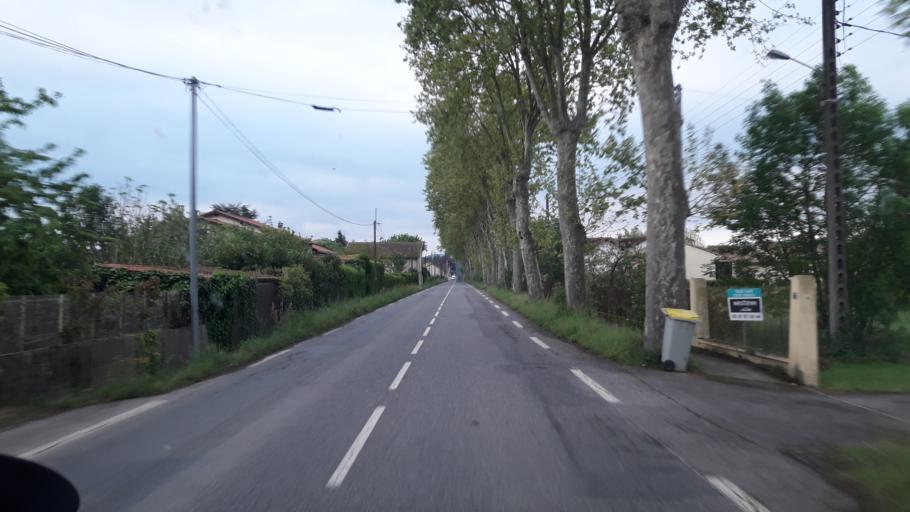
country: FR
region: Midi-Pyrenees
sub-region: Departement de la Haute-Garonne
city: Cazeres
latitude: 43.2177
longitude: 1.0851
